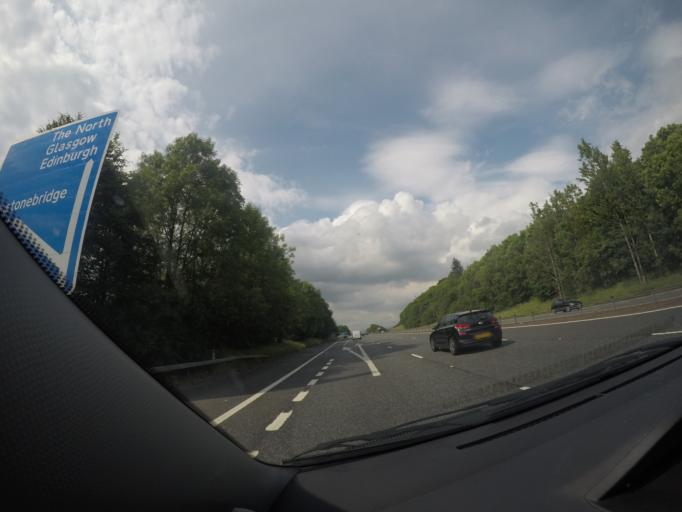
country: GB
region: Scotland
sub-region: Dumfries and Galloway
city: Lochmaben
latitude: 55.2139
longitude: -3.4130
